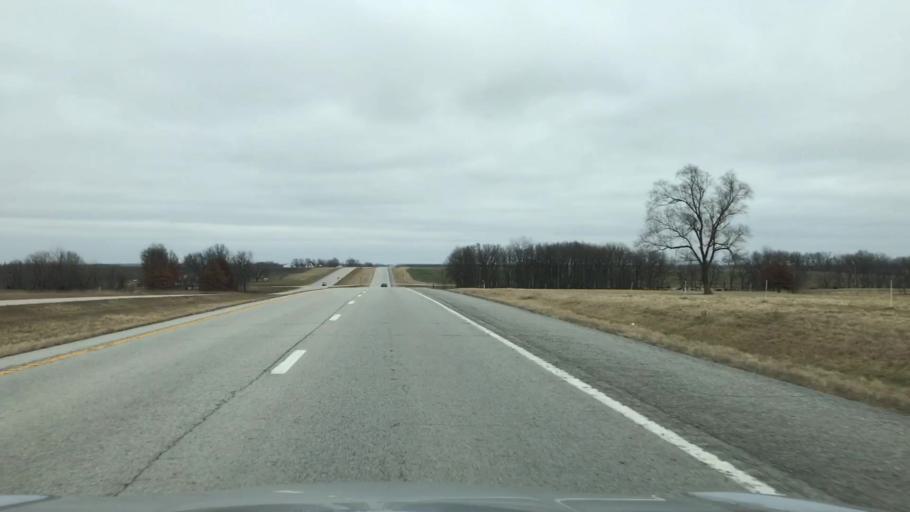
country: US
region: Missouri
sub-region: Livingston County
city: Chillicothe
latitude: 39.7760
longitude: -93.4867
